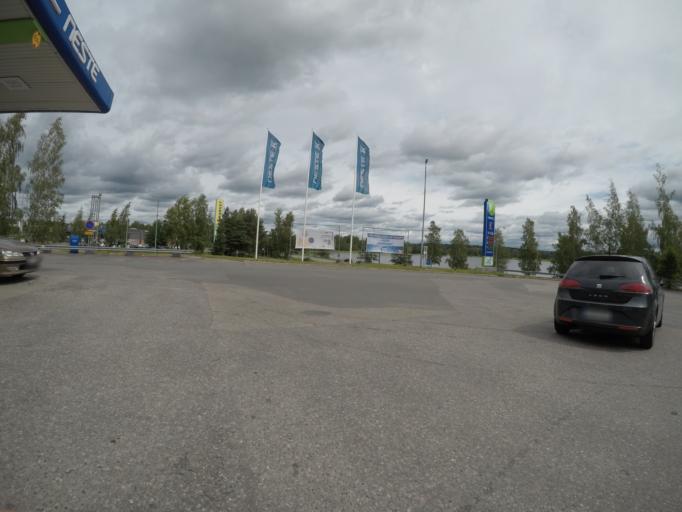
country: FI
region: Haeme
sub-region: Haemeenlinna
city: Haemeenlinna
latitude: 61.0052
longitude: 24.5061
